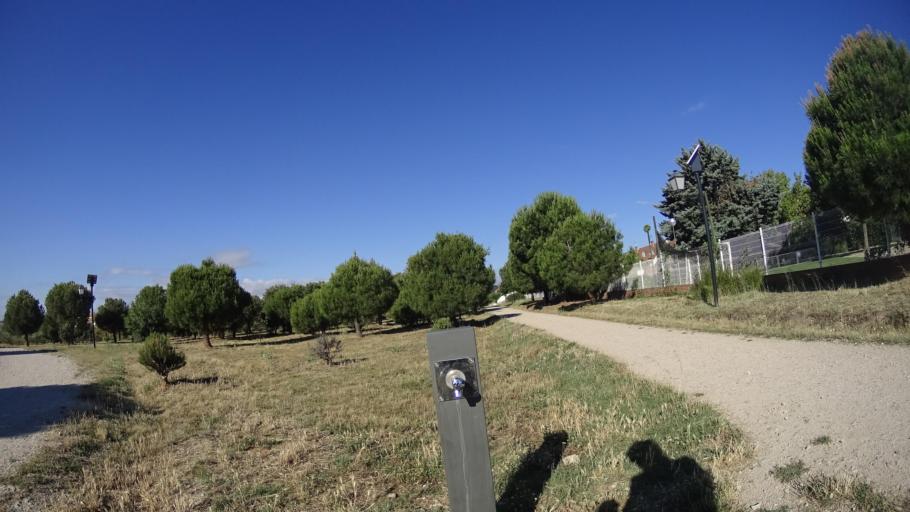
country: ES
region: Madrid
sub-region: Provincia de Madrid
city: Las Matas
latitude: 40.5527
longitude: -3.8872
